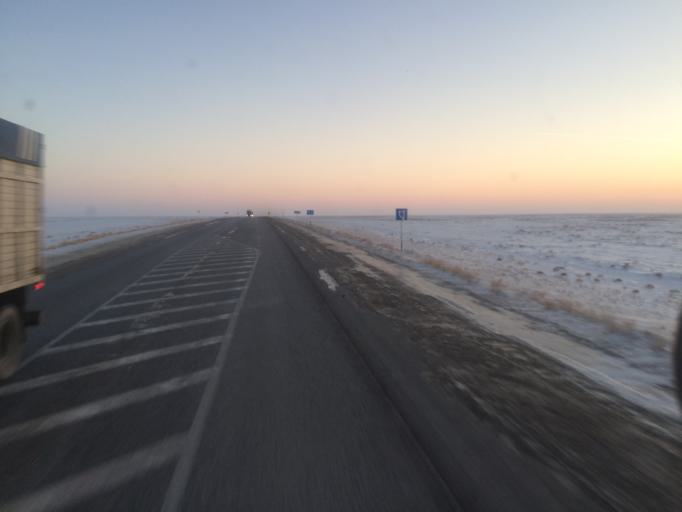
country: KZ
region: Qyzylorda
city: Sekseuil
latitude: 47.4433
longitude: 61.5380
